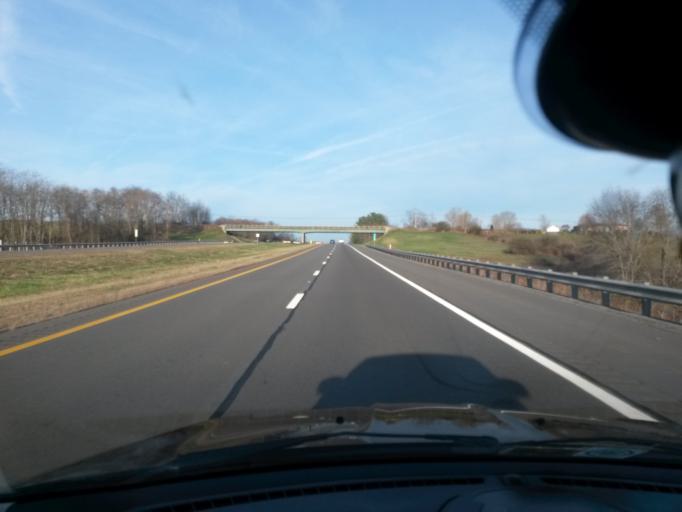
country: US
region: West Virginia
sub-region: Greenbrier County
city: Lewisburg
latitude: 37.8413
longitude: -80.4682
